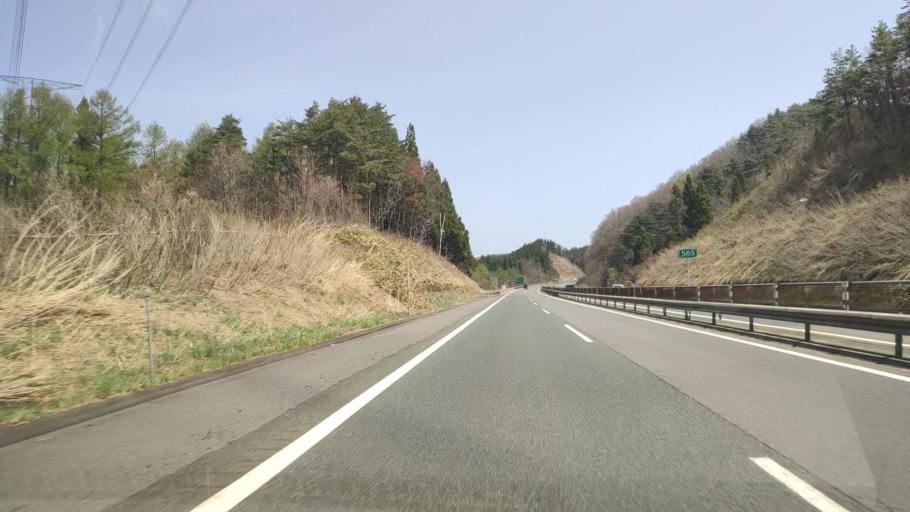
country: JP
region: Iwate
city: Ichinohe
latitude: 40.1122
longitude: 141.0738
